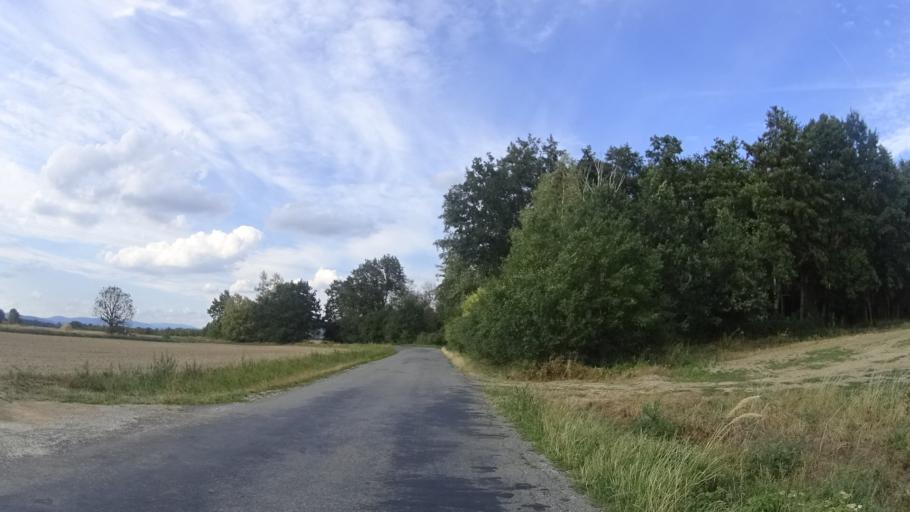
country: CZ
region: Olomoucky
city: Dubicko
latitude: 49.8118
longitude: 16.9427
